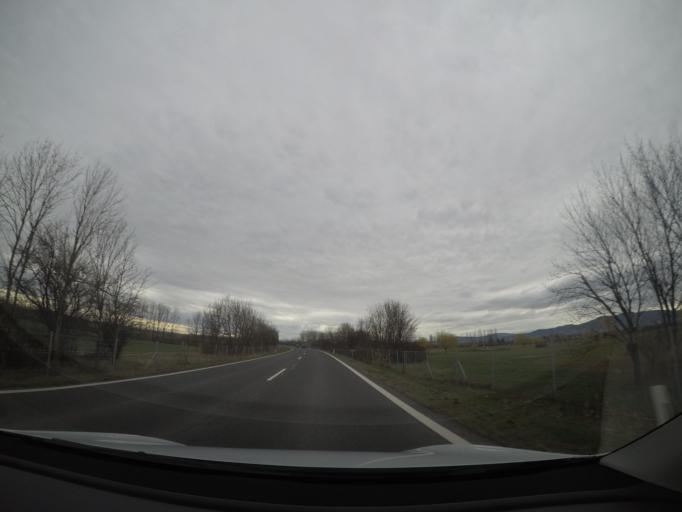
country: AT
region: Lower Austria
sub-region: Politischer Bezirk Modling
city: Munchendorf
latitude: 48.0368
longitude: 16.3658
